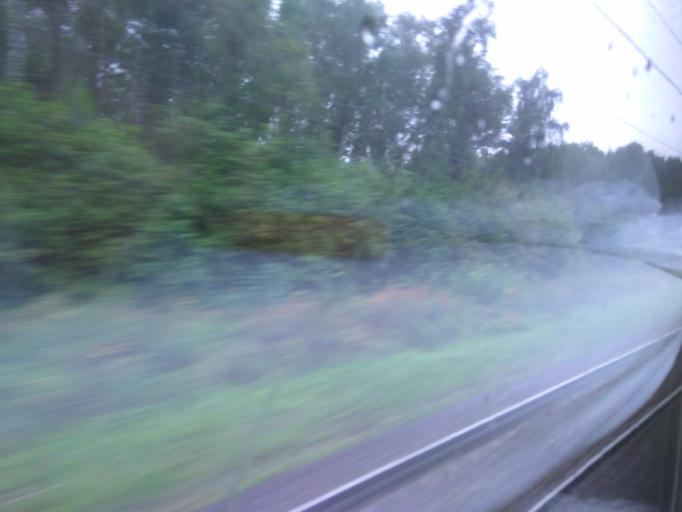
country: RU
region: Moskovskaya
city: Ozherel'ye
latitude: 54.8228
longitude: 38.2588
